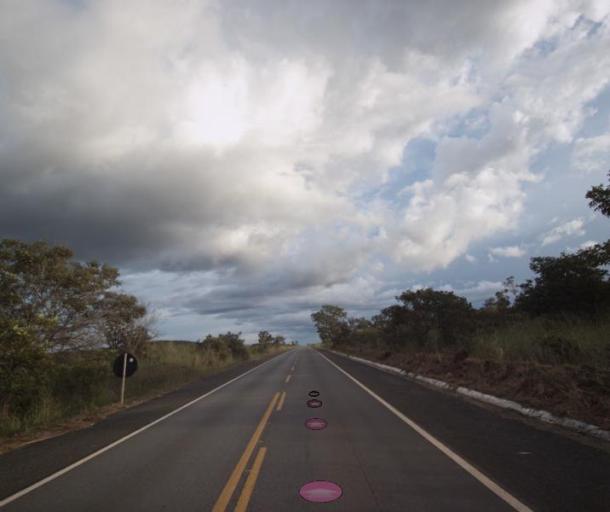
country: BR
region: Goias
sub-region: Barro Alto
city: Barro Alto
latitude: -14.8523
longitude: -48.6390
